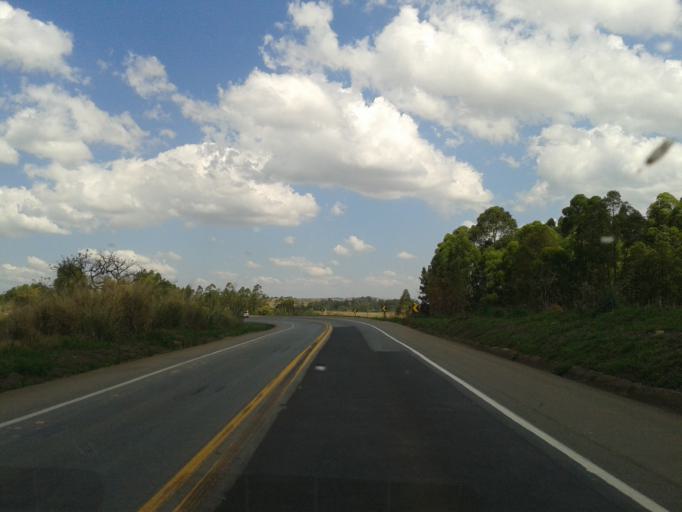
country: BR
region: Minas Gerais
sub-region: Campos Altos
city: Campos Altos
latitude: -19.6795
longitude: -46.0432
